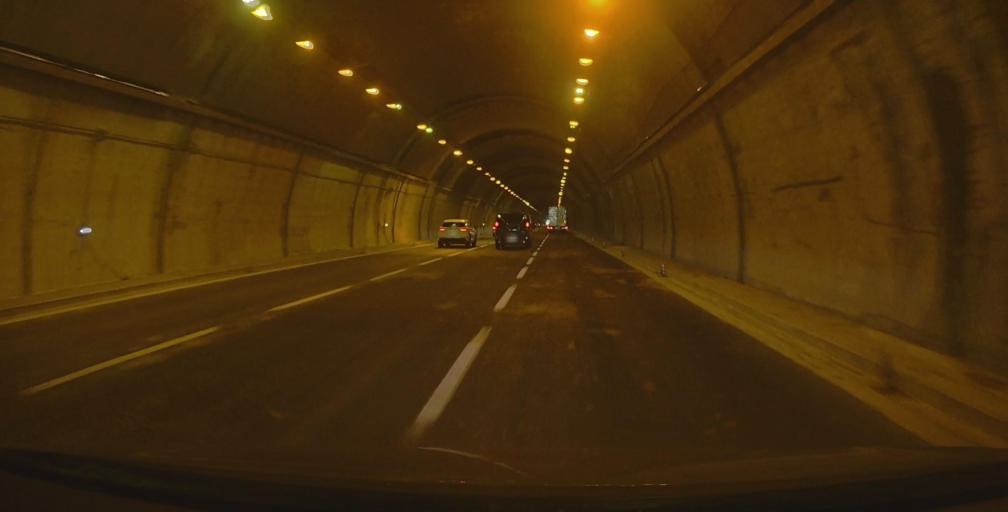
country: IT
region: Campania
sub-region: Provincia di Salerno
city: Lanzara
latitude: 40.7741
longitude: 14.6528
